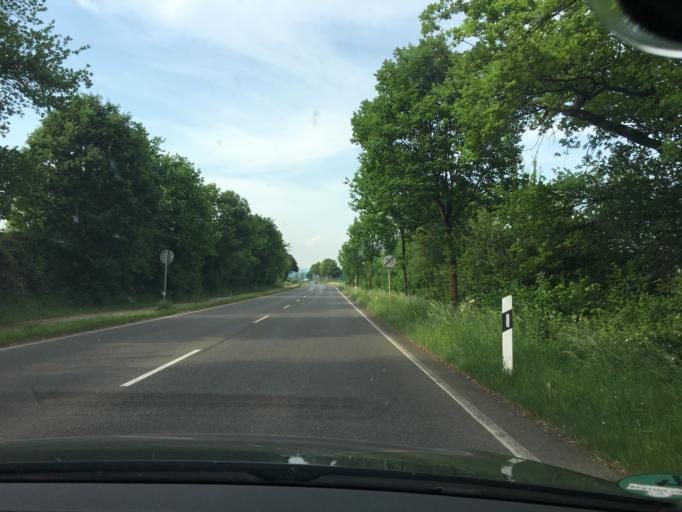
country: DE
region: North Rhine-Westphalia
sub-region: Regierungsbezirk Koln
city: Nideggen
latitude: 50.7008
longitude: 6.4885
